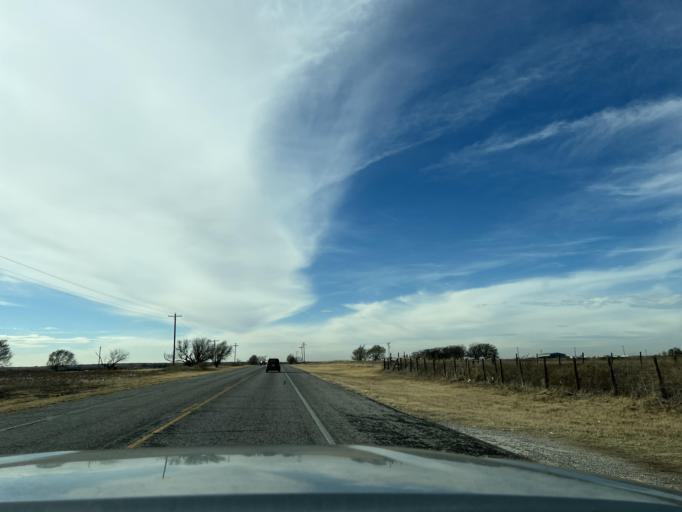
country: US
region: Texas
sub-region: Fisher County
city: Roby
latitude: 32.7587
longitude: -100.2859
